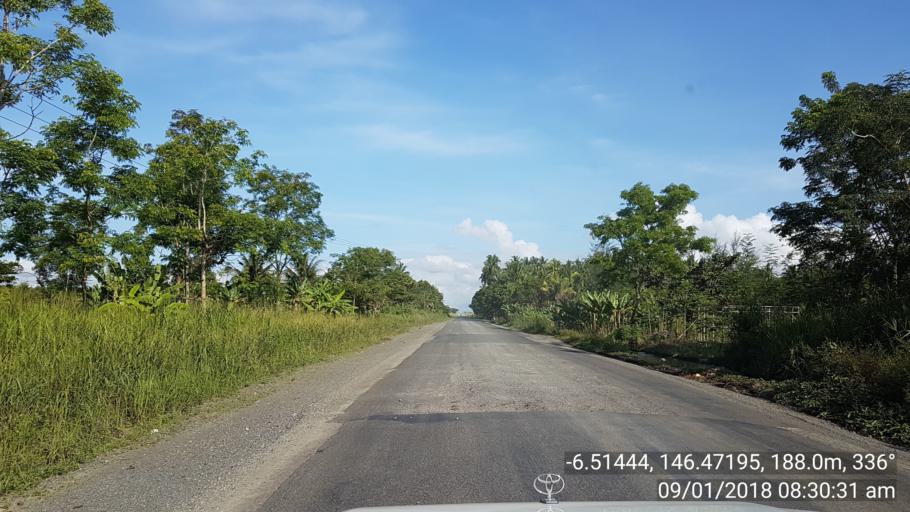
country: PG
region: Morobe
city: Lae
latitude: -6.5144
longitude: 146.4720
